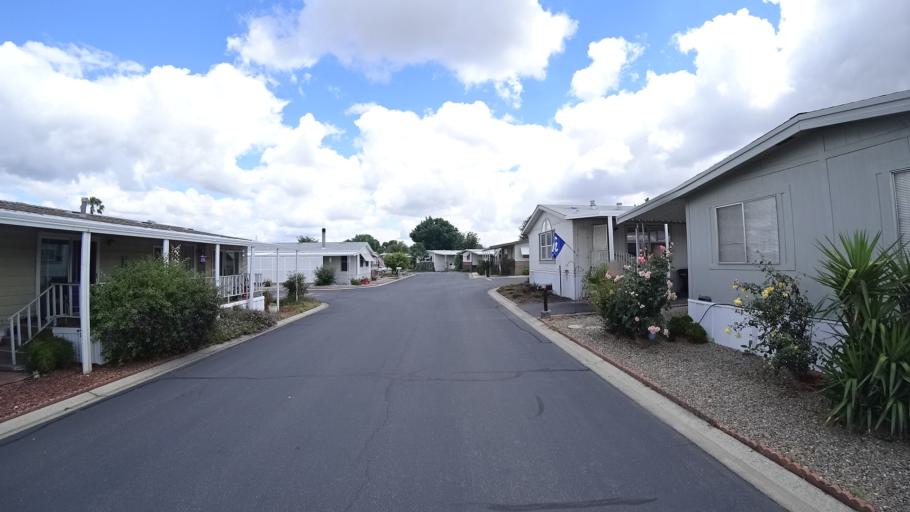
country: US
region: California
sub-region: Kings County
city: Hanford
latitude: 36.3439
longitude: -119.6317
